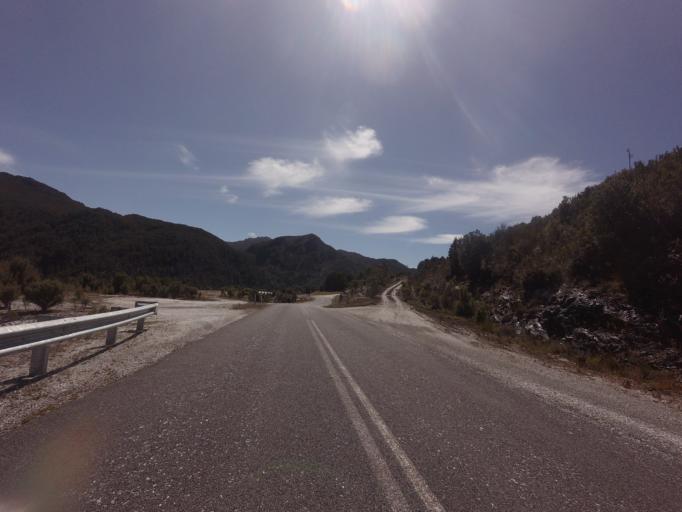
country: AU
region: Tasmania
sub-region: West Coast
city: Queenstown
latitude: -42.7345
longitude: 145.9758
